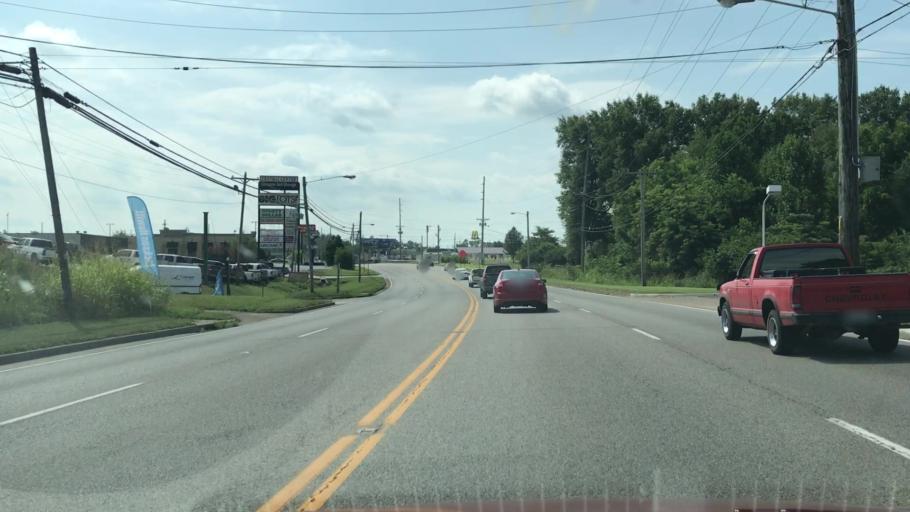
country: US
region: Kentucky
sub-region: Barren County
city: Glasgow
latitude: 37.0121
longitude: -85.9254
